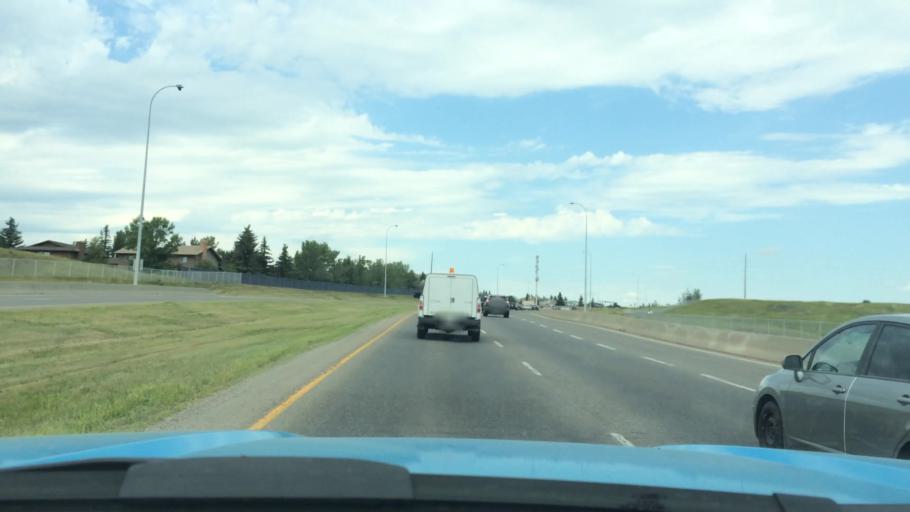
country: CA
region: Alberta
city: Calgary
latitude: 51.1220
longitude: -114.1343
